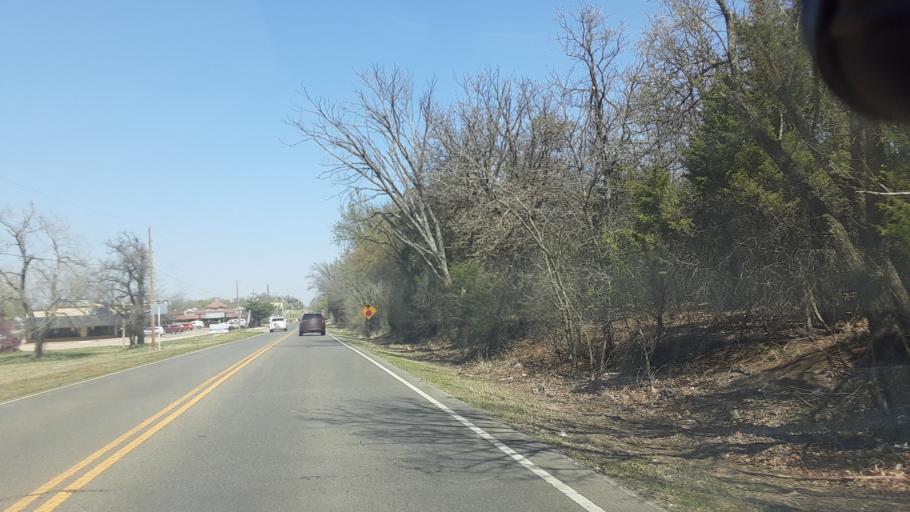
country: US
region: Oklahoma
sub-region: Oklahoma County
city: Edmond
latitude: 35.7233
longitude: -97.4783
